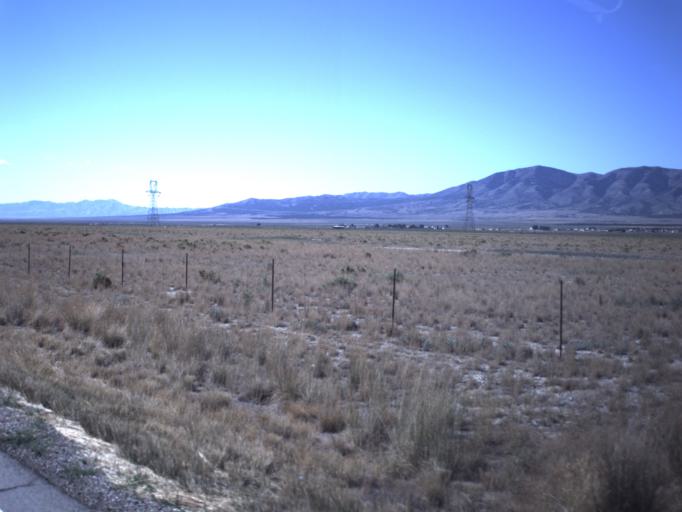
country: US
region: Utah
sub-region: Tooele County
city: Tooele
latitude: 40.3613
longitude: -112.4142
